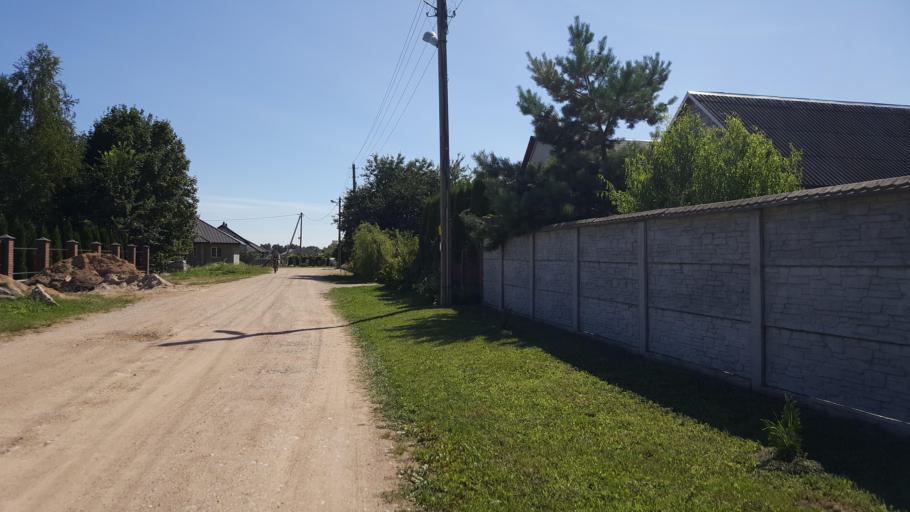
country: BY
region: Brest
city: Charnawchytsy
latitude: 52.2105
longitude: 23.7513
